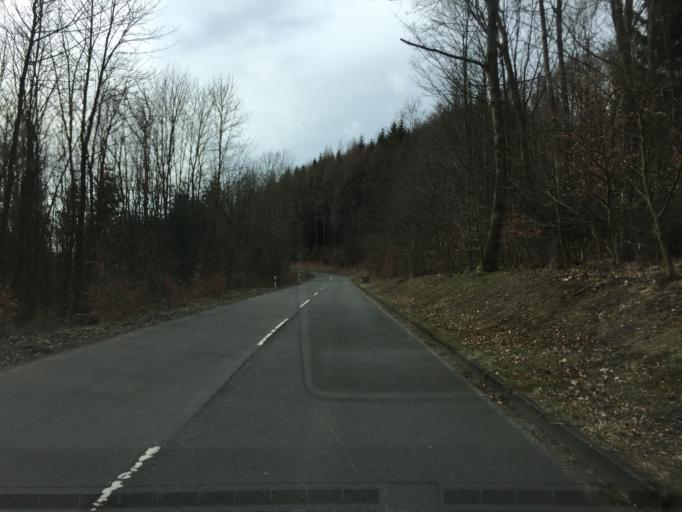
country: DE
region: North Rhine-Westphalia
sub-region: Regierungsbezirk Detmold
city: Detmold
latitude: 51.9121
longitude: 8.8472
